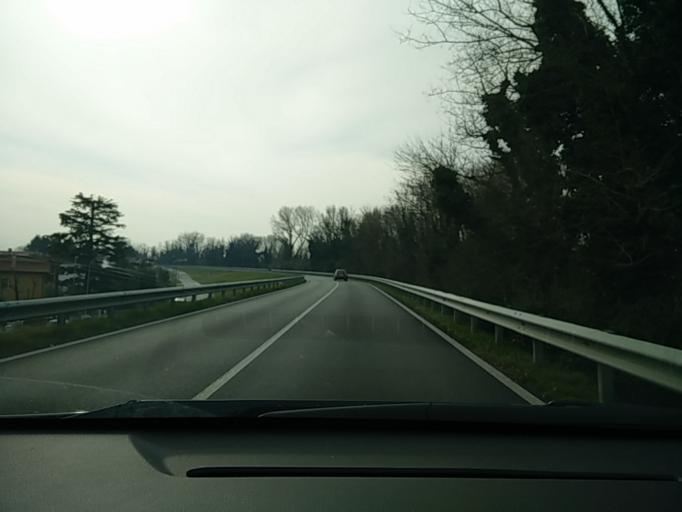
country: IT
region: Veneto
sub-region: Provincia di Venezia
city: San Dona di Piave
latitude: 45.6192
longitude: 12.5730
